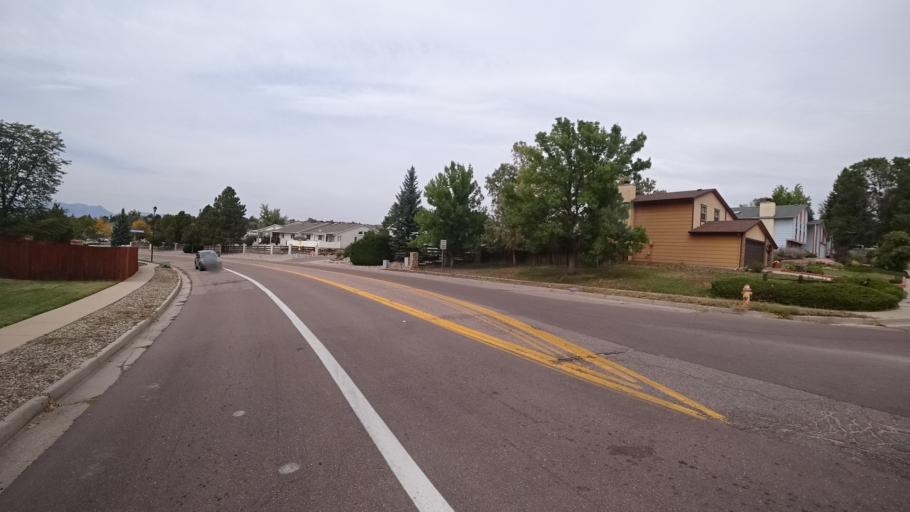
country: US
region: Colorado
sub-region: El Paso County
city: Cimarron Hills
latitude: 38.9052
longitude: -104.7355
